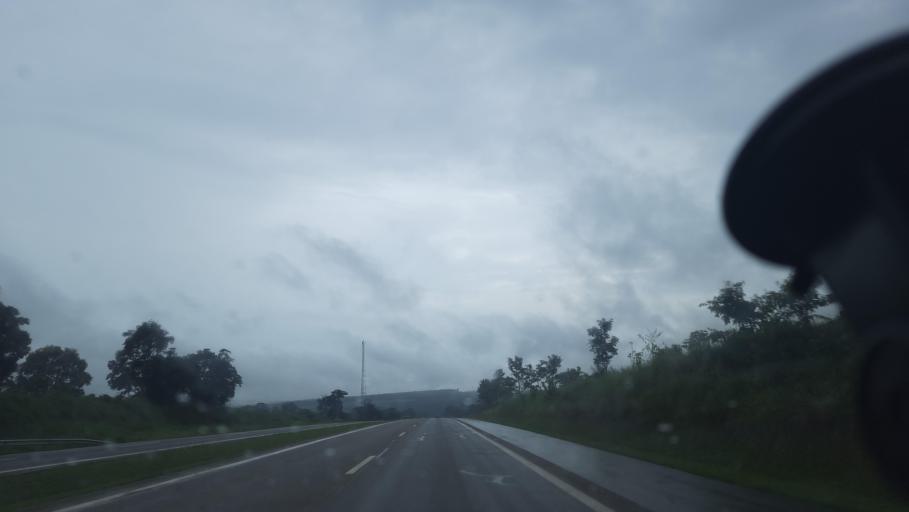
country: BR
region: Sao Paulo
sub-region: Casa Branca
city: Casa Branca
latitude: -21.8158
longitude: -47.0645
